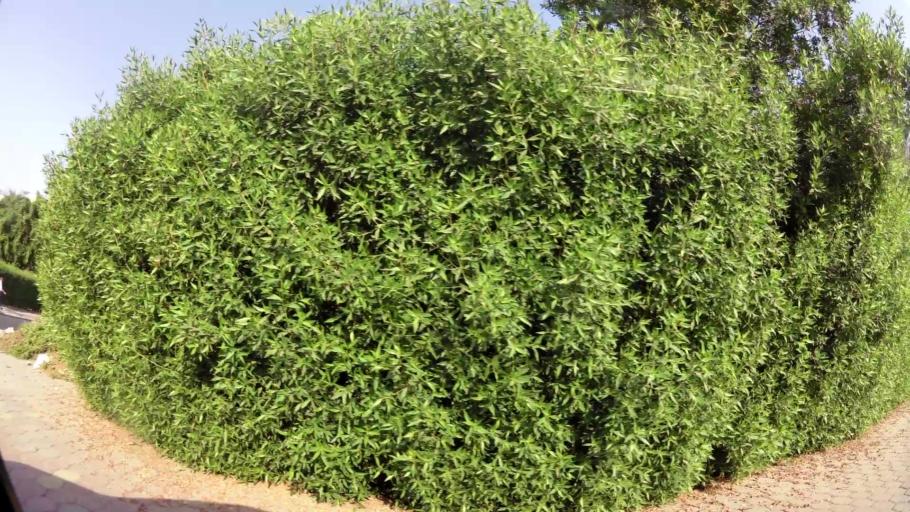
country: KW
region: Al Asimah
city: Ad Dasmah
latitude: 29.3664
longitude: 48.0060
